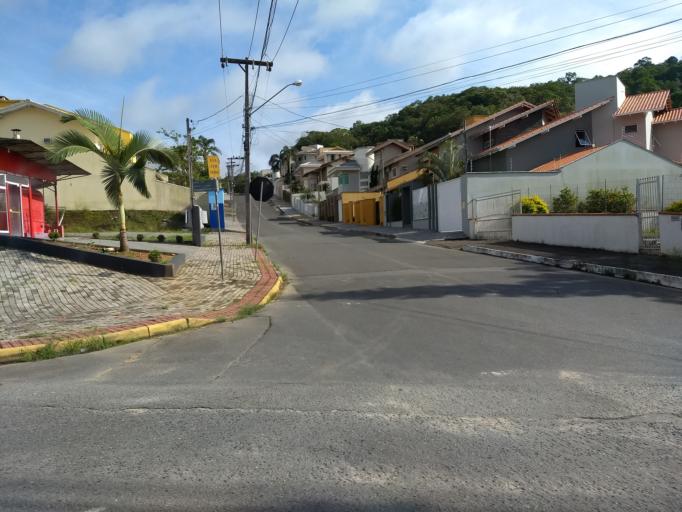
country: BR
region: Santa Catarina
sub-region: Jaragua Do Sul
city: Jaragua do Sul
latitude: -26.4693
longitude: -49.0963
